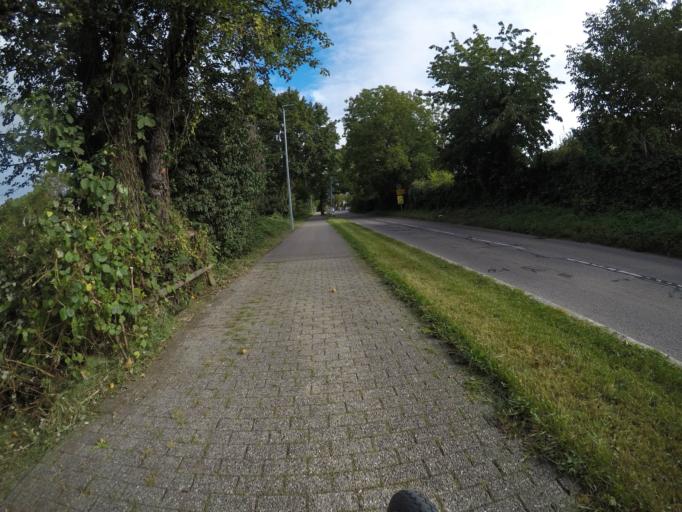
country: DE
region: Baden-Wuerttemberg
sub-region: Regierungsbezirk Stuttgart
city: Stuttgart Muehlhausen
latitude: 48.8296
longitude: 9.2159
